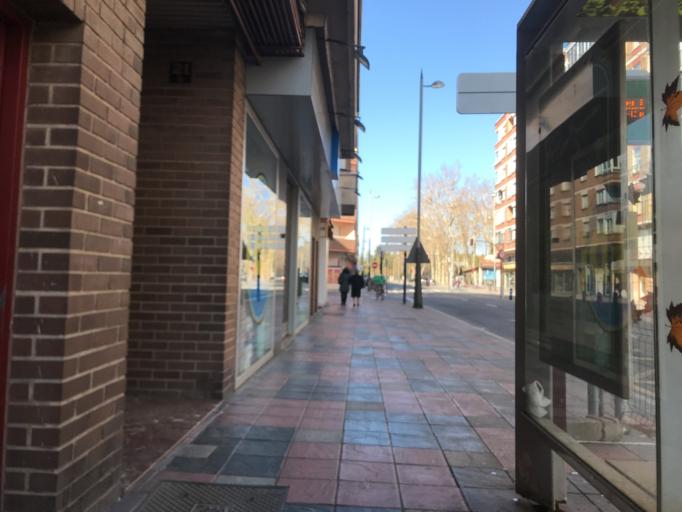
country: ES
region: Basque Country
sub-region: Provincia de Alava
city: Gasteiz / Vitoria
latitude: 42.8553
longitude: -2.6736
